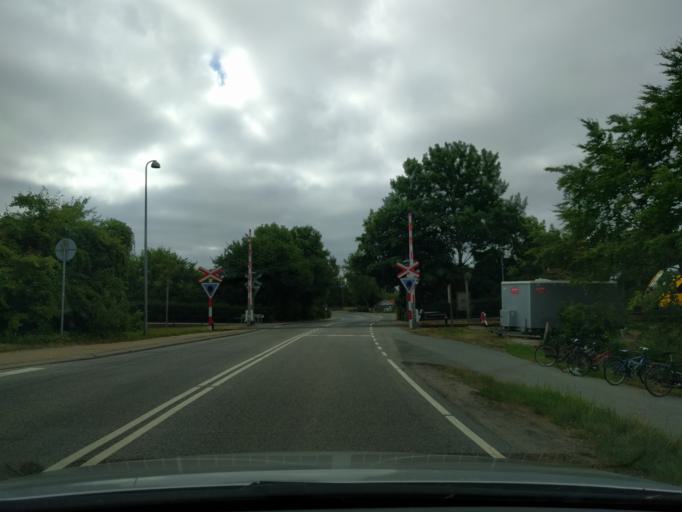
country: DK
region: Capital Region
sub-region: Helsingor Kommune
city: Espergaerde
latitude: 56.0025
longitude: 12.5325
